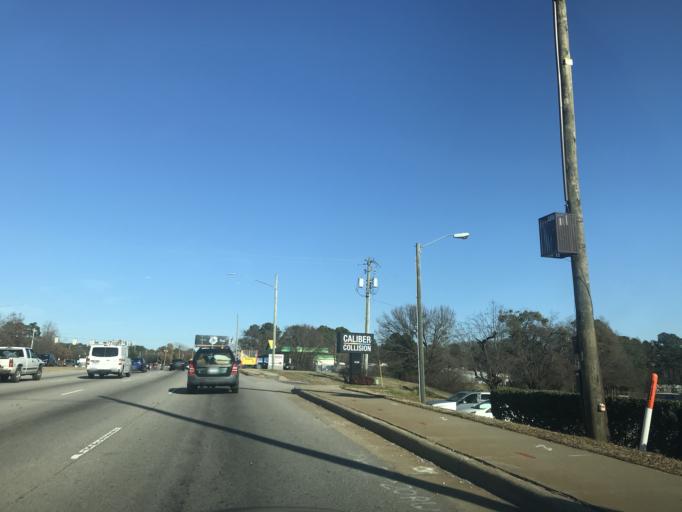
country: US
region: North Carolina
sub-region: Wake County
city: Raleigh
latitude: 35.8213
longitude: -78.5903
